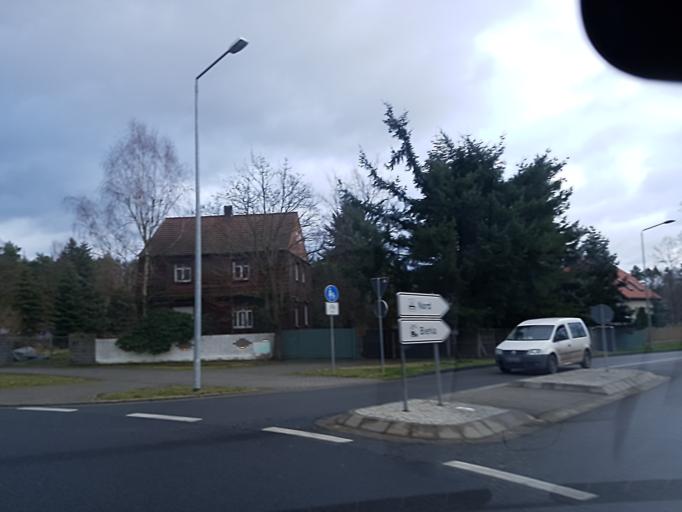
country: DE
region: Brandenburg
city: Elsterwerda
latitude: 51.4789
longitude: 13.5054
